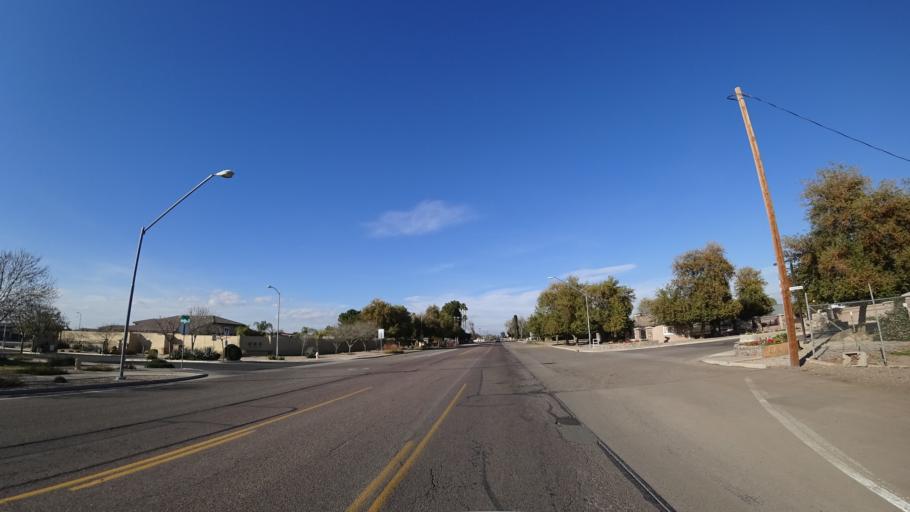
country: US
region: Arizona
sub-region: Maricopa County
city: Peoria
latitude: 33.5474
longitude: -112.2378
